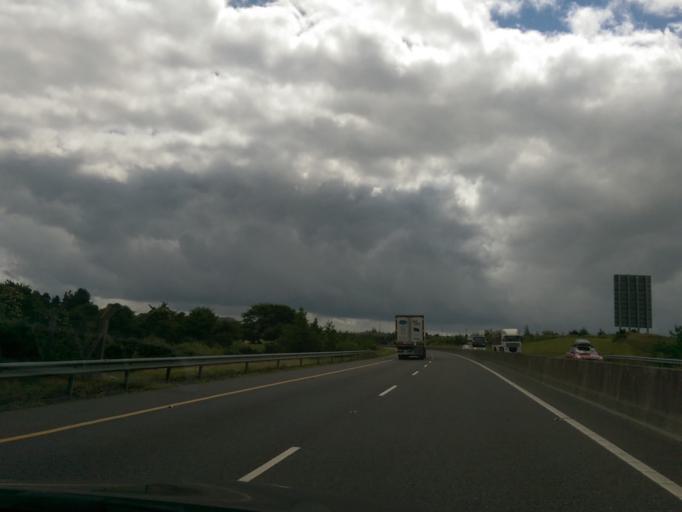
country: IE
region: Munster
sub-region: County Cork
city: Mitchelstown
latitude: 52.2256
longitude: -8.2876
